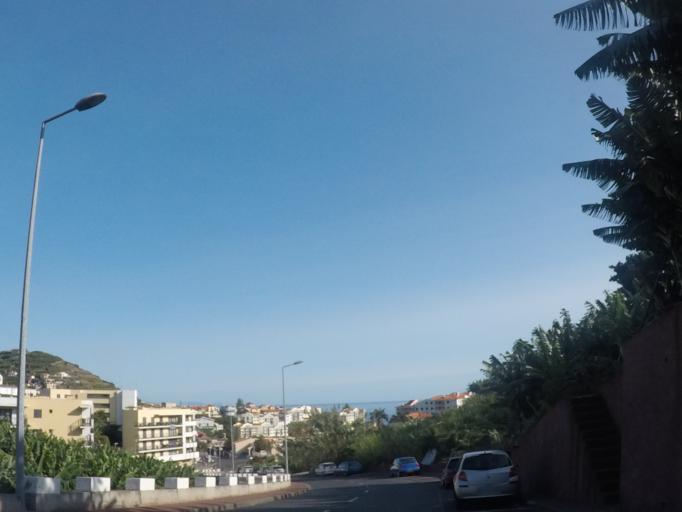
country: PT
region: Madeira
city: Camara de Lobos
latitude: 32.6541
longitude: -16.9860
